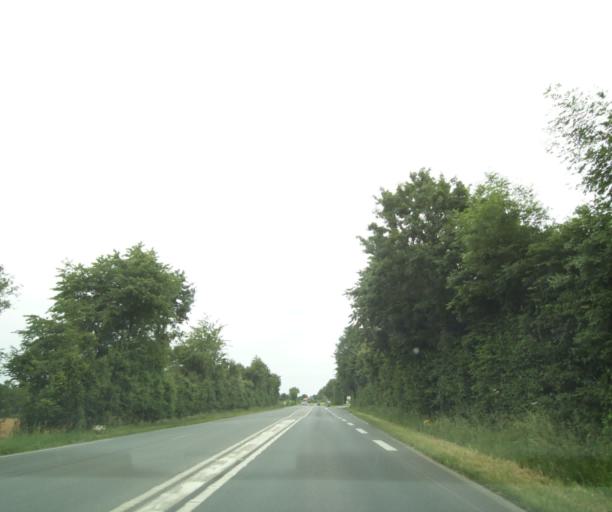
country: FR
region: Poitou-Charentes
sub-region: Departement des Deux-Sevres
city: Champdeniers-Saint-Denis
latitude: 46.4660
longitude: -0.3706
